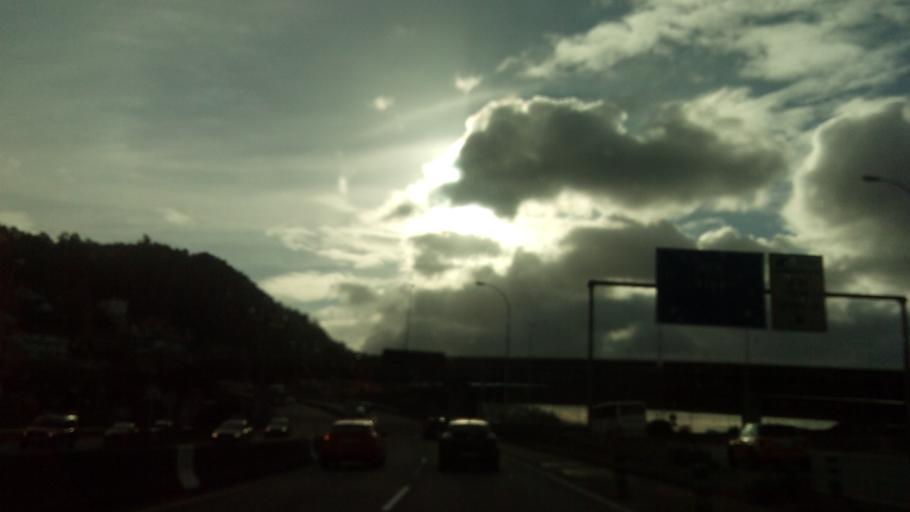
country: ES
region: Galicia
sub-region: Provincia de Pontevedra
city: Vigo
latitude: 42.2600
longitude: -8.6743
